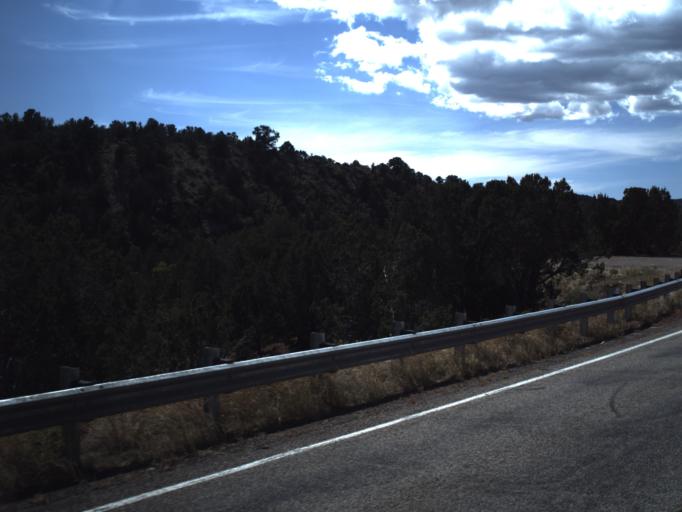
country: US
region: Utah
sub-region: Washington County
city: Enterprise
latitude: 37.5410
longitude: -113.6638
